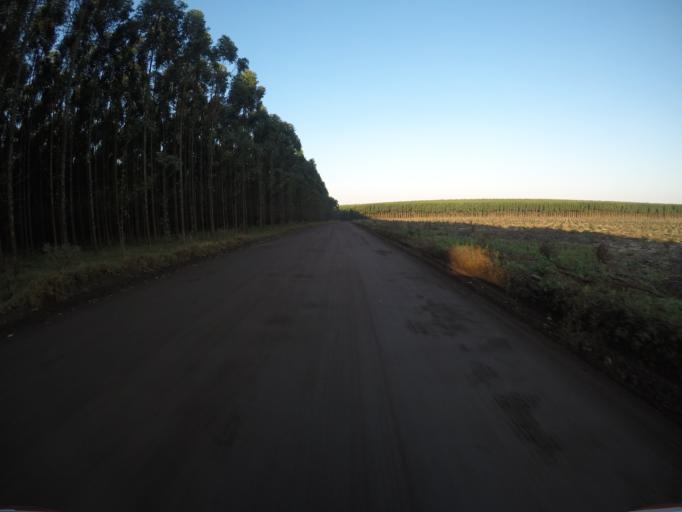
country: ZA
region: KwaZulu-Natal
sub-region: uThungulu District Municipality
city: KwaMbonambi
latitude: -28.6732
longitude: 32.1037
